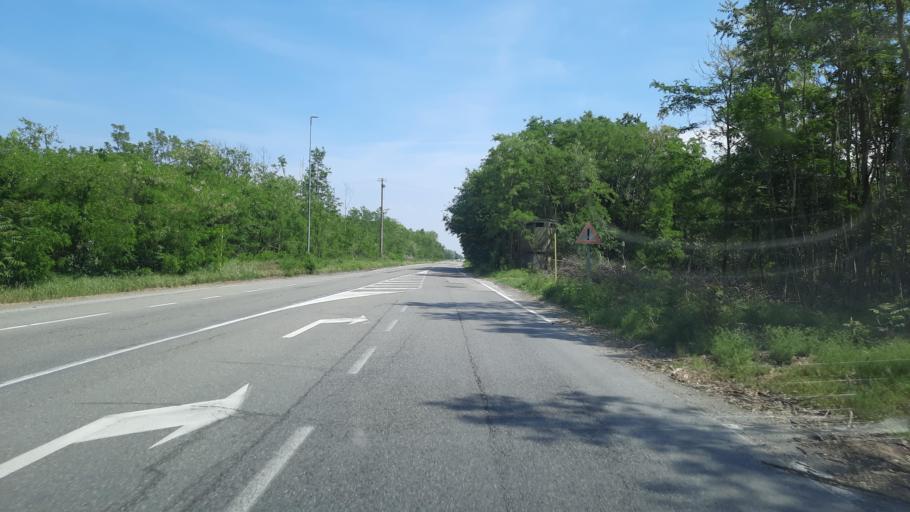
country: IT
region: Lombardy
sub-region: Provincia di Pavia
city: Cergnago
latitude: 45.2341
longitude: 8.8020
